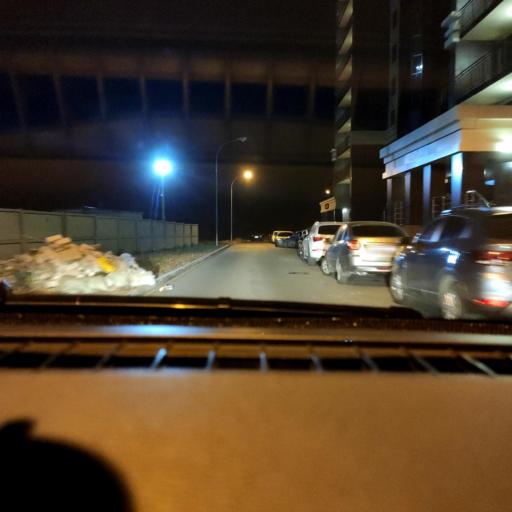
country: RU
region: Voronezj
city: Podgornoye
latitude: 51.7212
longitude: 39.1810
